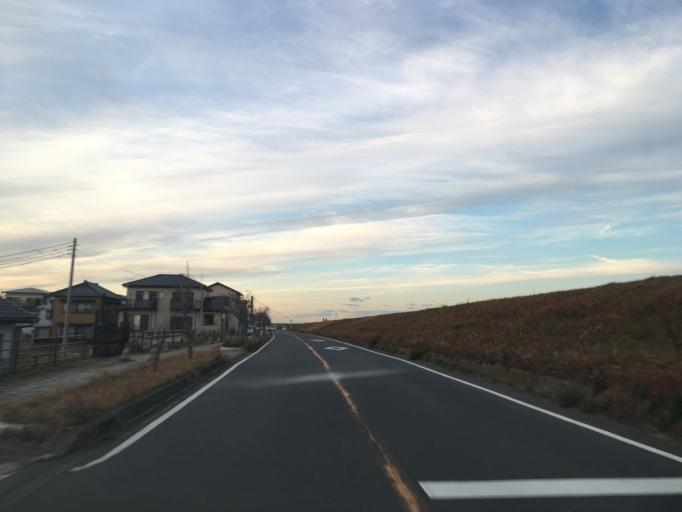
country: JP
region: Chiba
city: Katori-shi
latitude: 35.9023
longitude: 140.4997
